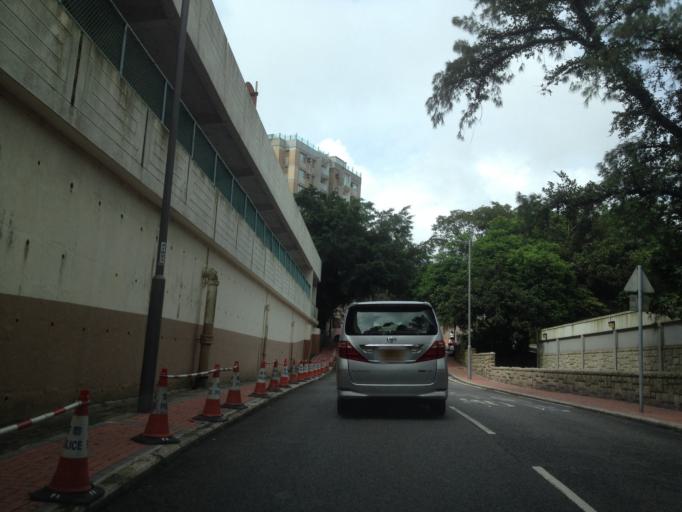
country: HK
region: Central and Western
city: Central
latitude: 22.2665
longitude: 114.1618
